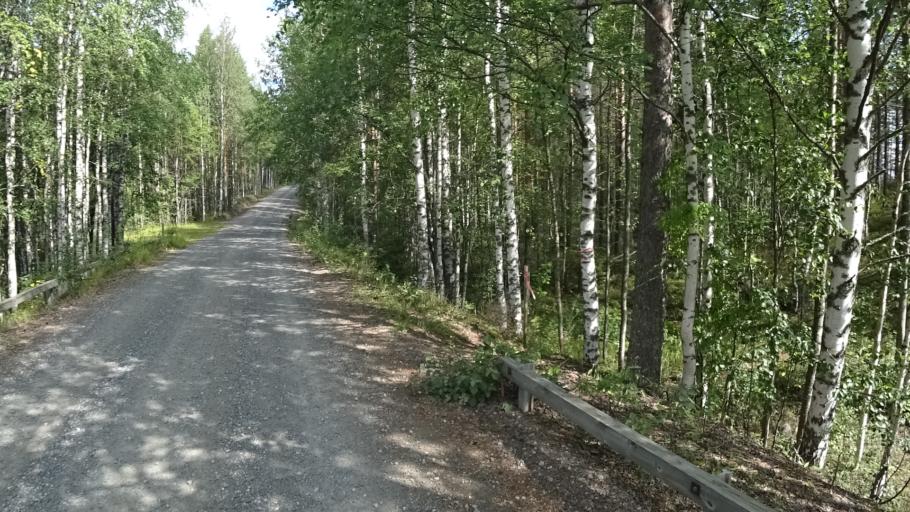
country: FI
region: North Karelia
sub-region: Joensuu
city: Ilomantsi
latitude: 62.6103
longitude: 31.1863
